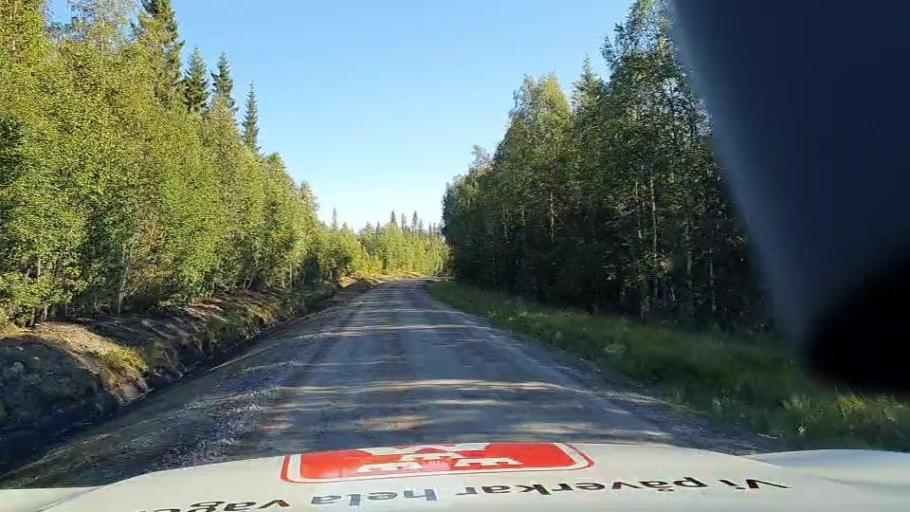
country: SE
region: Jaemtland
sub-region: Stroemsunds Kommun
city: Stroemsund
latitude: 64.5658
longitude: 15.0889
